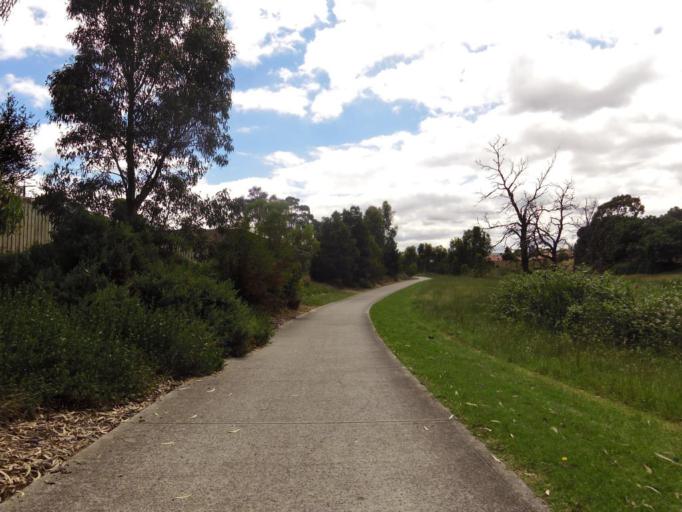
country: AU
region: Victoria
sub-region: Banyule
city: Bundoora
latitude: -37.6934
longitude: 145.0538
